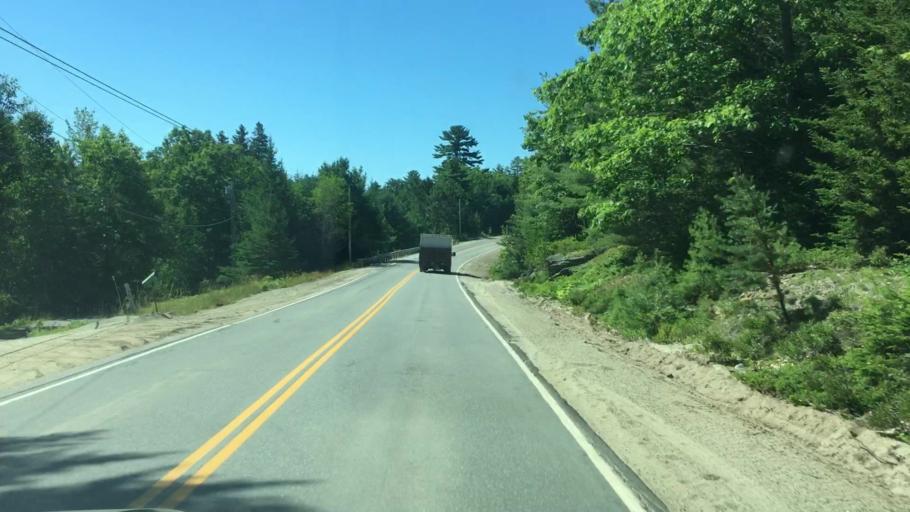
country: US
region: Maine
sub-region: Hancock County
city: Sedgwick
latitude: 44.3695
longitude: -68.5672
